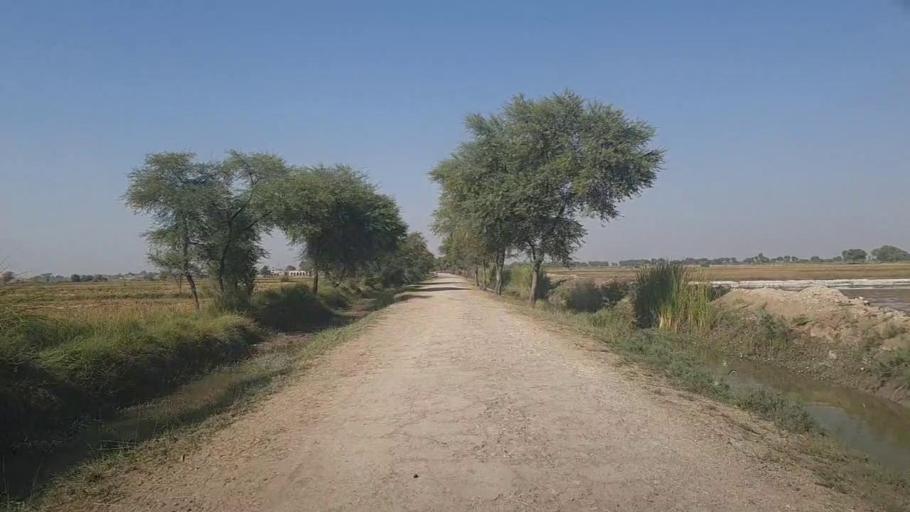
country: PK
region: Sindh
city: Thul
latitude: 28.3072
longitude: 68.7700
